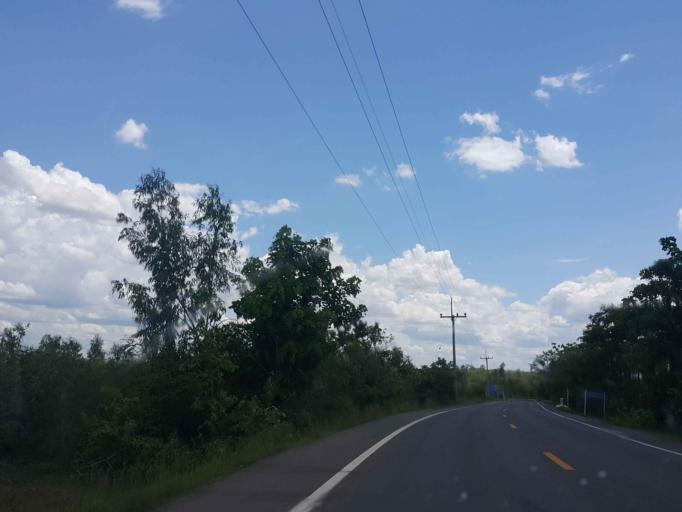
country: TH
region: Phrae
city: Nong Muang Khai
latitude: 18.1941
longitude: 100.2186
